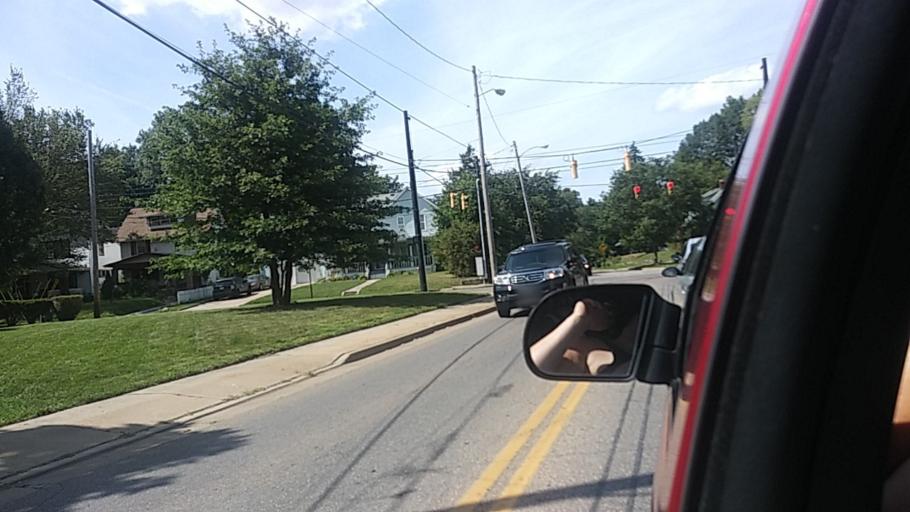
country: US
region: Ohio
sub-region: Summit County
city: Akron
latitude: 41.0785
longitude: -81.5485
